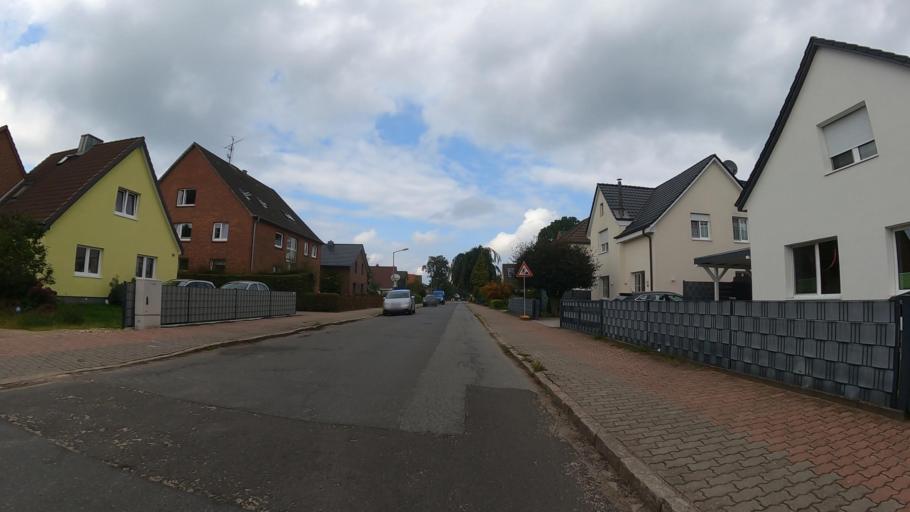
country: DE
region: Schleswig-Holstein
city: Tornesch
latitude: 53.7017
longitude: 9.7157
